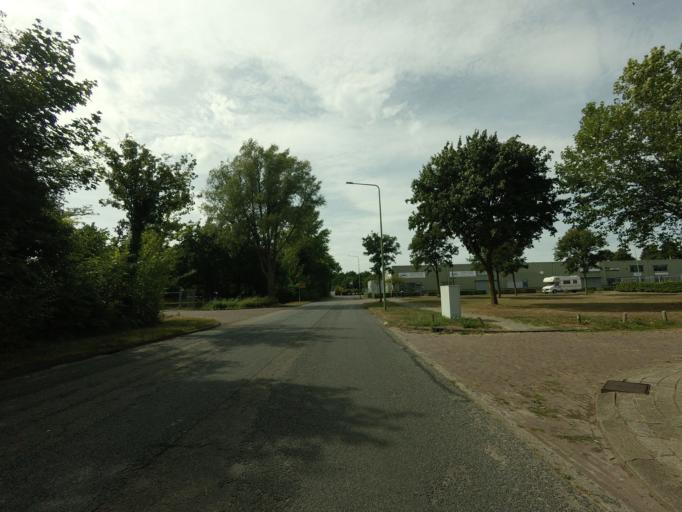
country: NL
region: Utrecht
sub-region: Gemeente Zeist
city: Zeist
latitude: 52.0878
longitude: 5.2126
